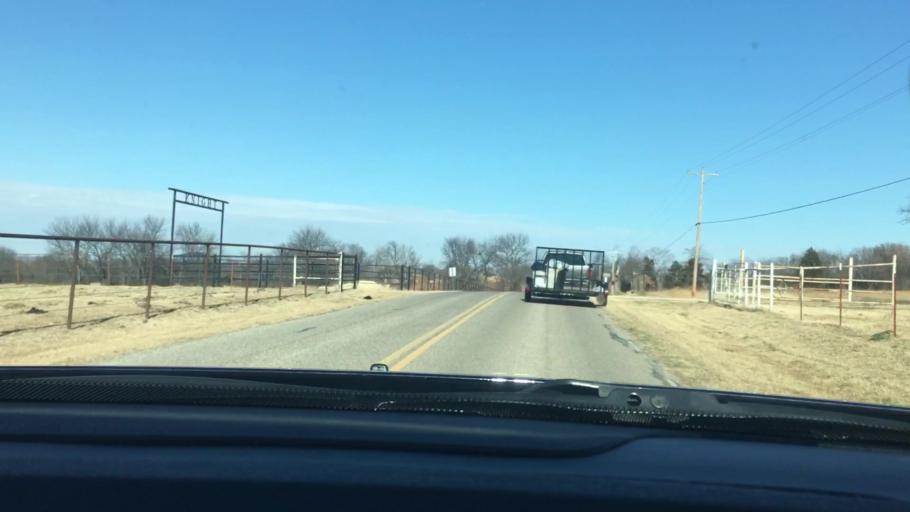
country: US
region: Oklahoma
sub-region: Murray County
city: Davis
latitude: 34.4823
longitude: -97.0556
